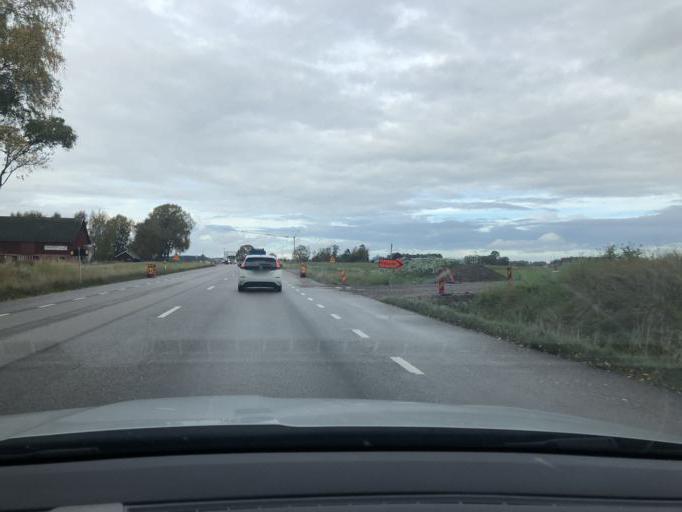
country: SE
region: Vaestra Goetaland
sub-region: Skara Kommun
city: Skara
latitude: 58.4157
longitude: 13.4665
